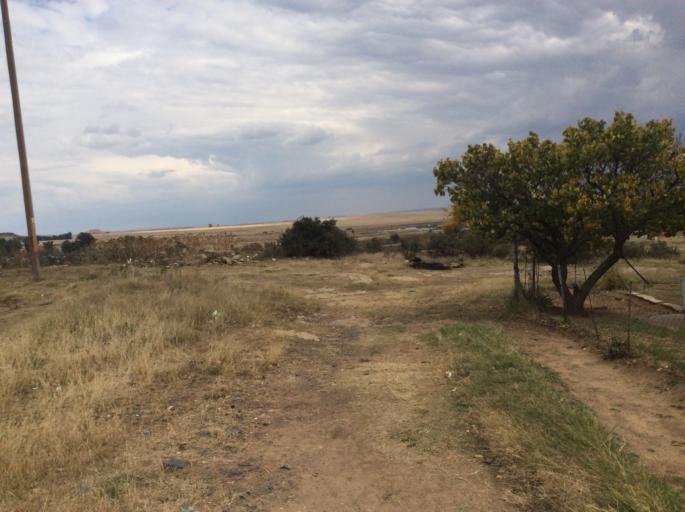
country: LS
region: Mafeteng
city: Mafeteng
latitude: -29.7213
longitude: 27.0282
